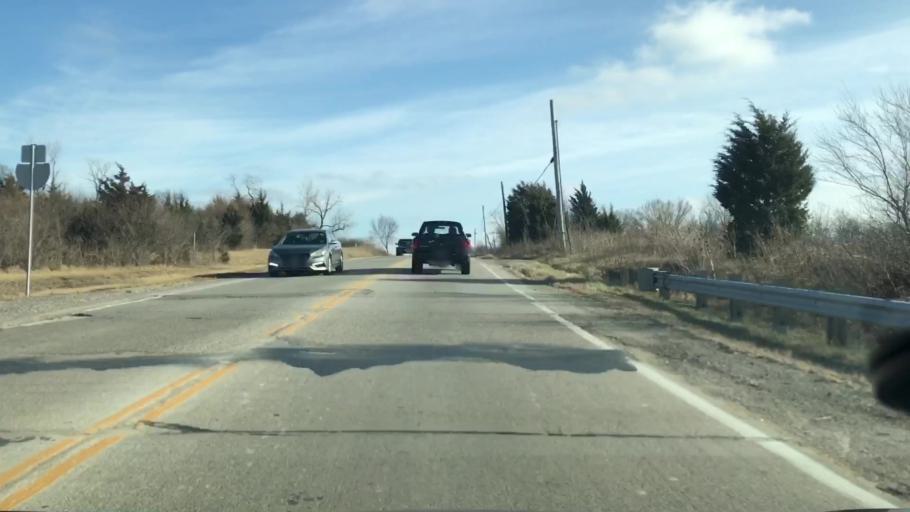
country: US
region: Ohio
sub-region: Greene County
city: Fairborn
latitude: 39.8149
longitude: -83.9971
